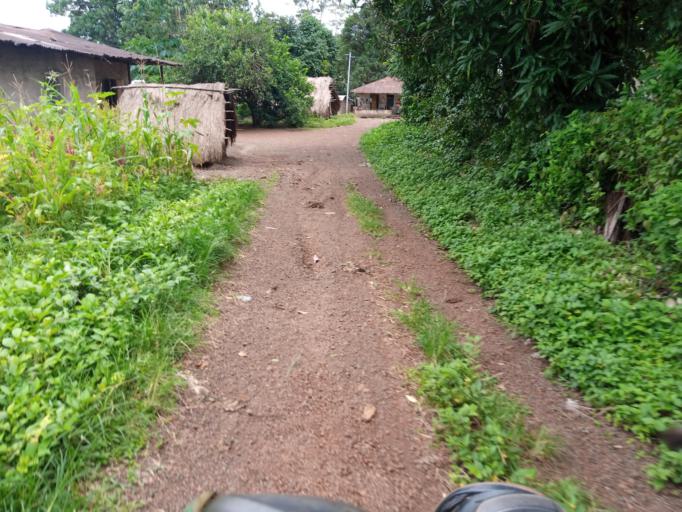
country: SL
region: Southern Province
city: Largo
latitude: 8.1998
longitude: -12.0647
